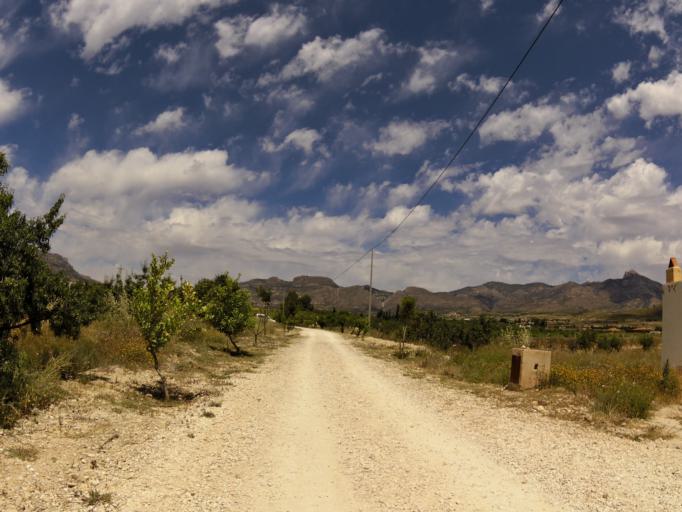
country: ES
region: Valencia
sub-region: Provincia de Alicante
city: Agost
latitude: 38.4416
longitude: -0.6506
